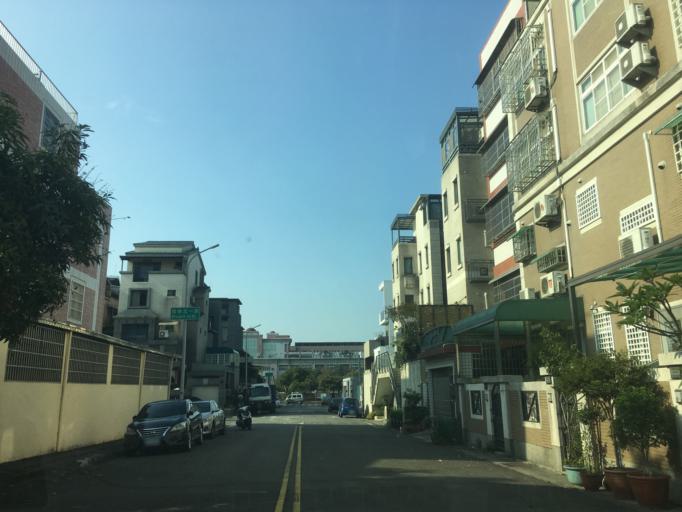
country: TW
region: Taiwan
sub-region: Taichung City
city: Taichung
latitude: 24.1964
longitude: 120.6768
